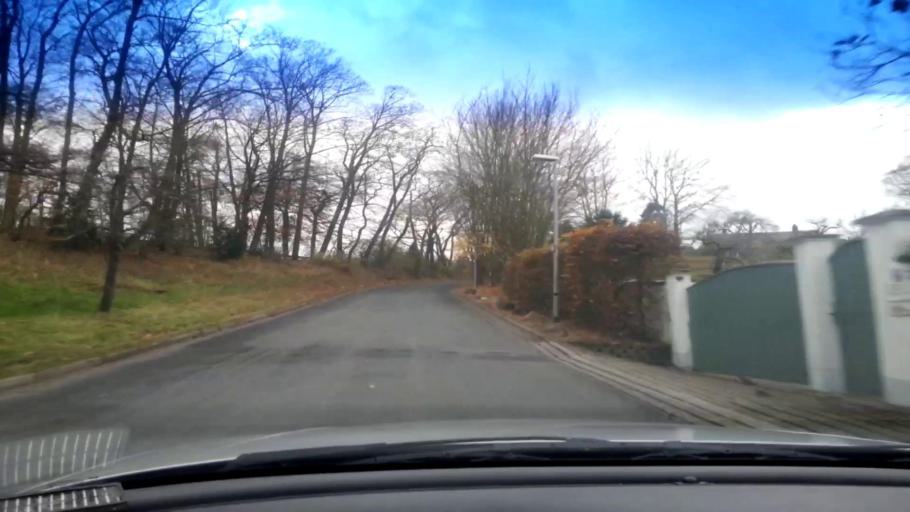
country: DE
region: Bavaria
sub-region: Upper Franconia
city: Bamberg
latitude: 49.8918
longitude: 10.8705
